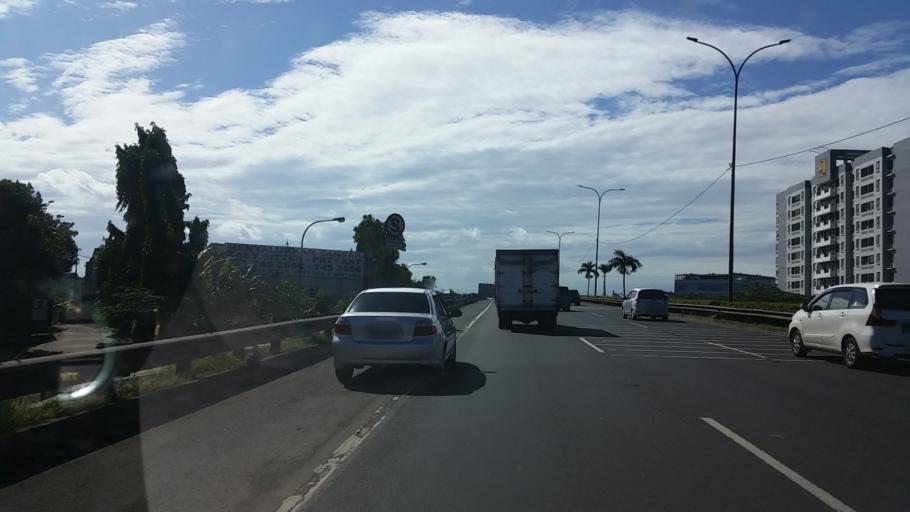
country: ID
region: Banten
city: South Tangerang
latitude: -6.2600
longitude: 106.7663
